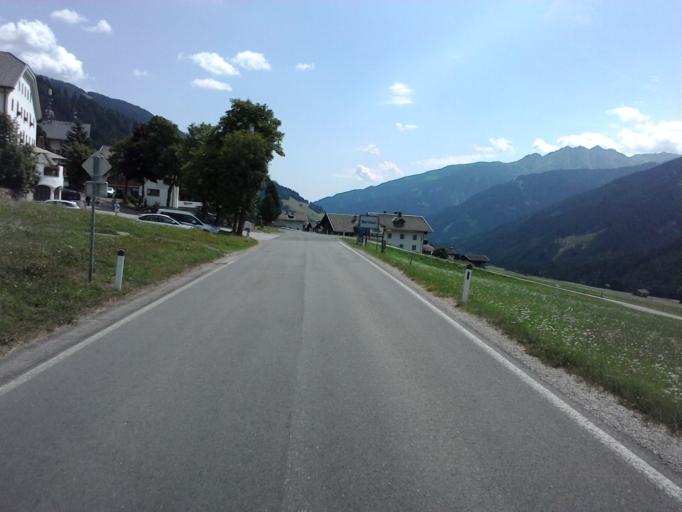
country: AT
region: Tyrol
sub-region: Politischer Bezirk Lienz
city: Obertilliach
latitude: 46.7084
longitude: 12.6110
